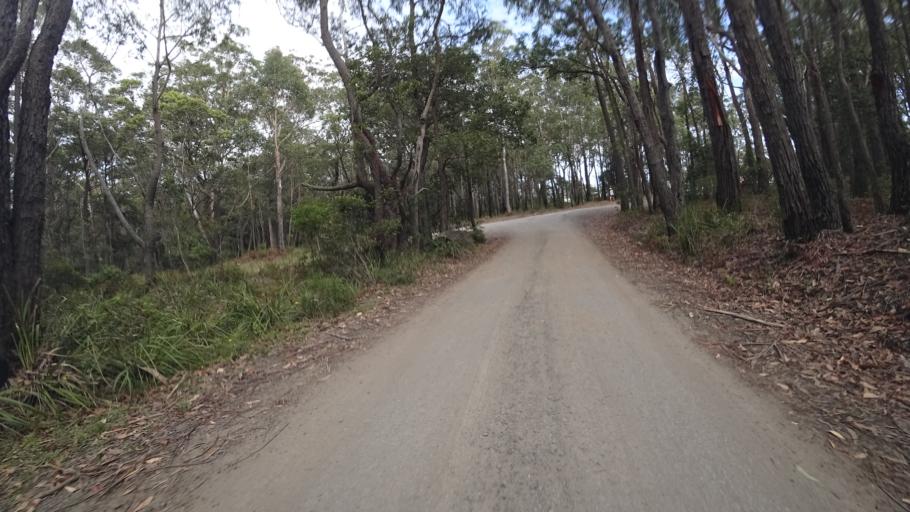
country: AU
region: New South Wales
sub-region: Shoalhaven Shire
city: Milton
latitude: -35.2378
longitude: 150.5293
